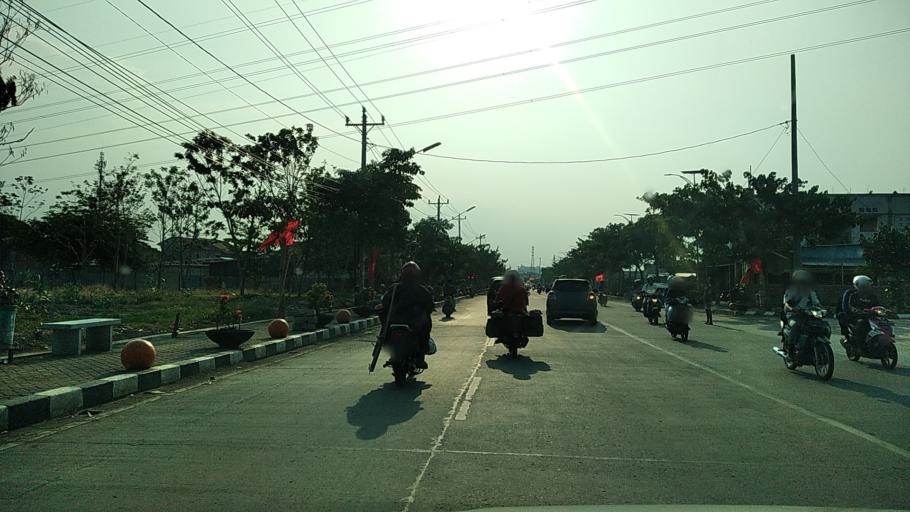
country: ID
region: Central Java
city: Semarang
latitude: -6.9857
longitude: 110.4448
